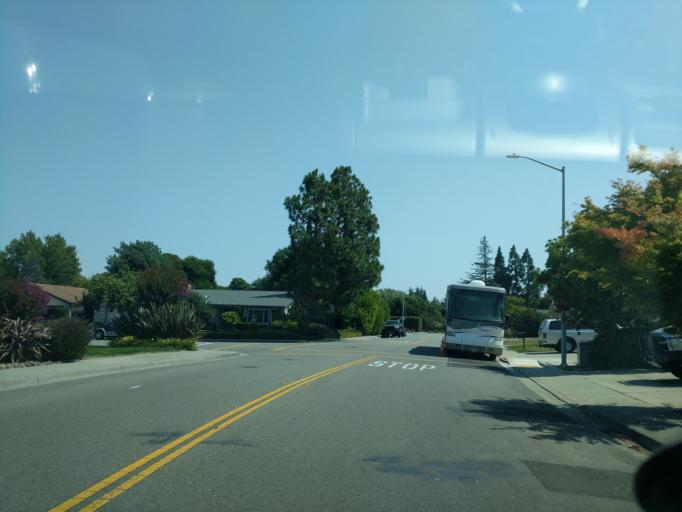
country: US
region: California
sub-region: Contra Costa County
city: San Ramon
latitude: 37.7711
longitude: -121.9844
